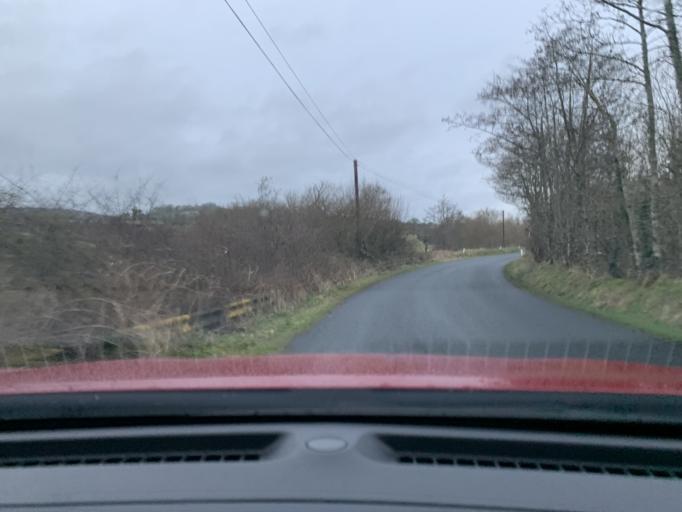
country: IE
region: Connaught
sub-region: Roscommon
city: Boyle
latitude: 54.0287
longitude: -8.3357
